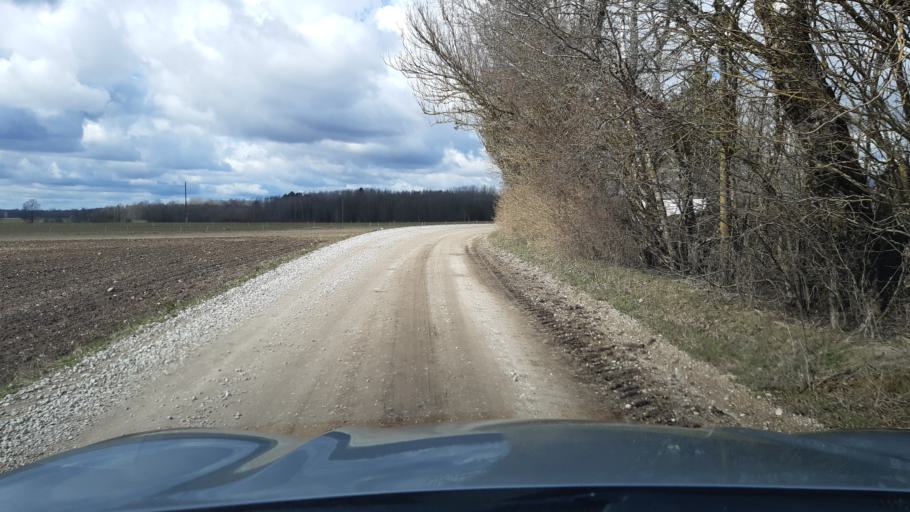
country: EE
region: Raplamaa
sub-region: Kehtna vald
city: Kehtna
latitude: 59.0614
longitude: 25.1016
